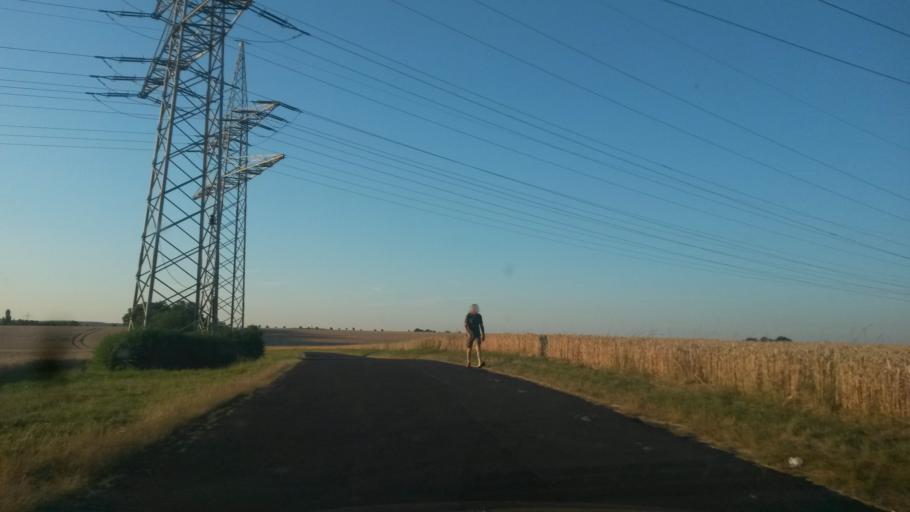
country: DE
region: Bavaria
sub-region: Regierungsbezirk Unterfranken
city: Wuerzburg
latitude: 49.8096
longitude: 9.9328
